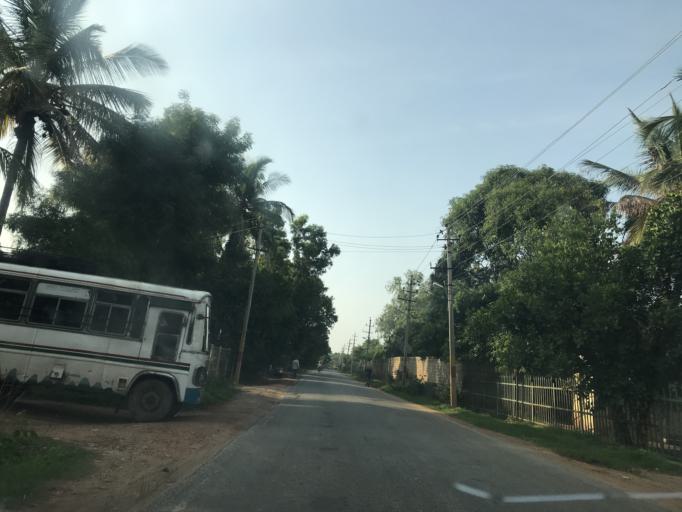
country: IN
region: Karnataka
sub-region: Bangalore Rural
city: Devanhalli
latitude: 13.1954
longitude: 77.6456
